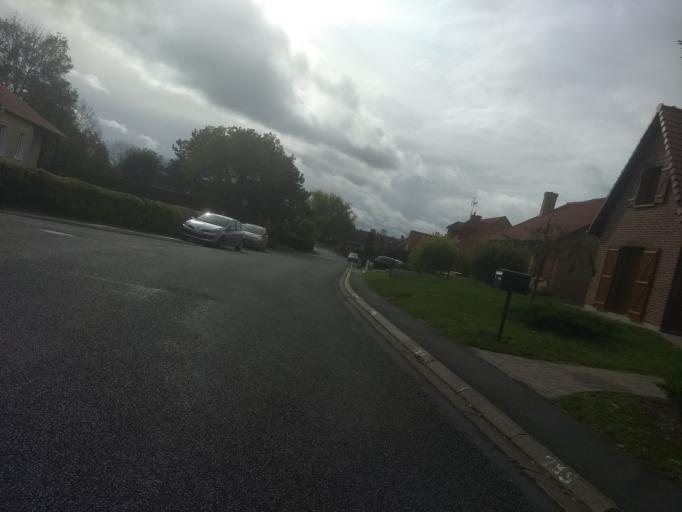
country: FR
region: Nord-Pas-de-Calais
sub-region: Departement du Pas-de-Calais
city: Anzin-Saint-Aubin
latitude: 50.3141
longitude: 2.7501
